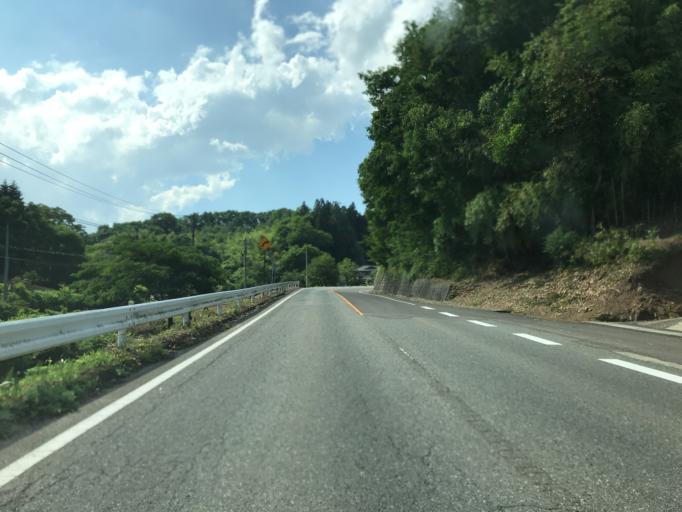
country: JP
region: Fukushima
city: Yanagawamachi-saiwaicho
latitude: 37.8107
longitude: 140.5969
